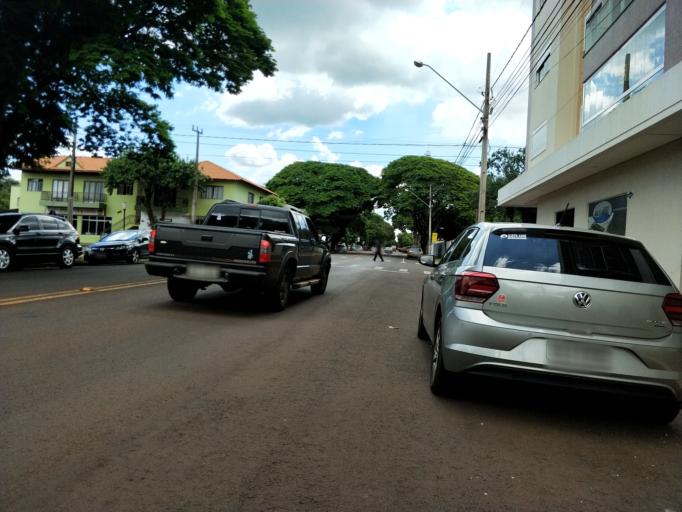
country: BR
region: Parana
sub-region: Marechal Candido Rondon
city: Marechal Candido Rondon
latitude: -24.5599
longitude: -54.0536
